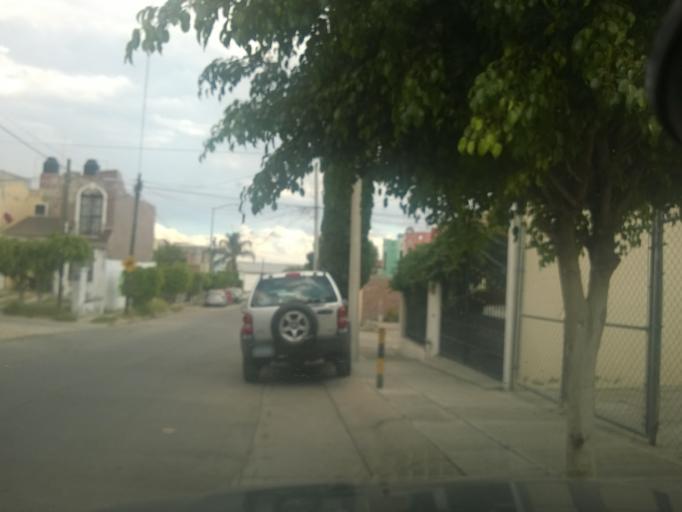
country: MX
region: Guanajuato
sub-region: Leon
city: Ejido la Joya
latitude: 21.1296
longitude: -101.7156
